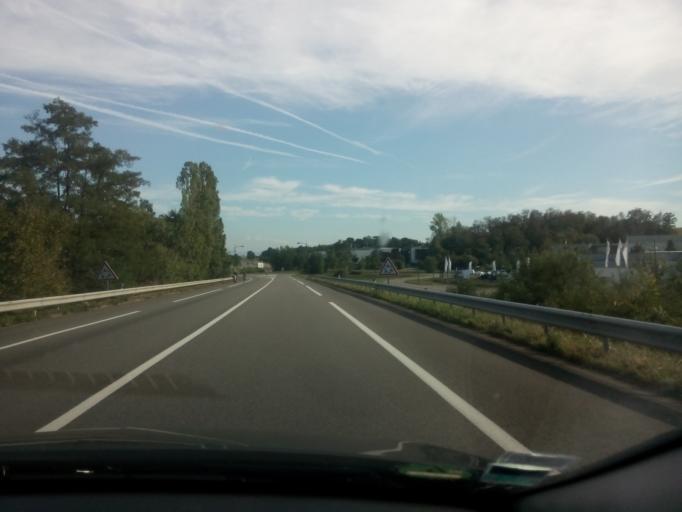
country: FR
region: Alsace
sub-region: Departement du Bas-Rhin
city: Wissembourg
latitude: 49.0236
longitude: 7.9644
